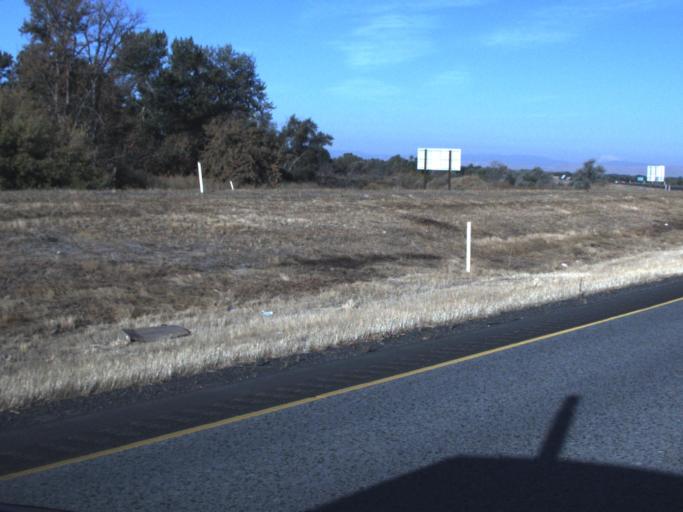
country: US
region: Washington
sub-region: Yakima County
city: Zillah
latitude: 46.4105
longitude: -120.2892
